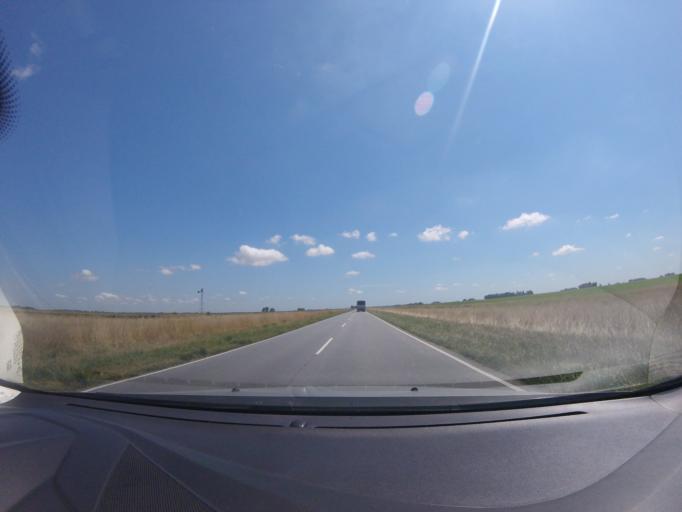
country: AR
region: Buenos Aires
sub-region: Partido de Rauch
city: Rauch
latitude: -37.0394
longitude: -59.0011
